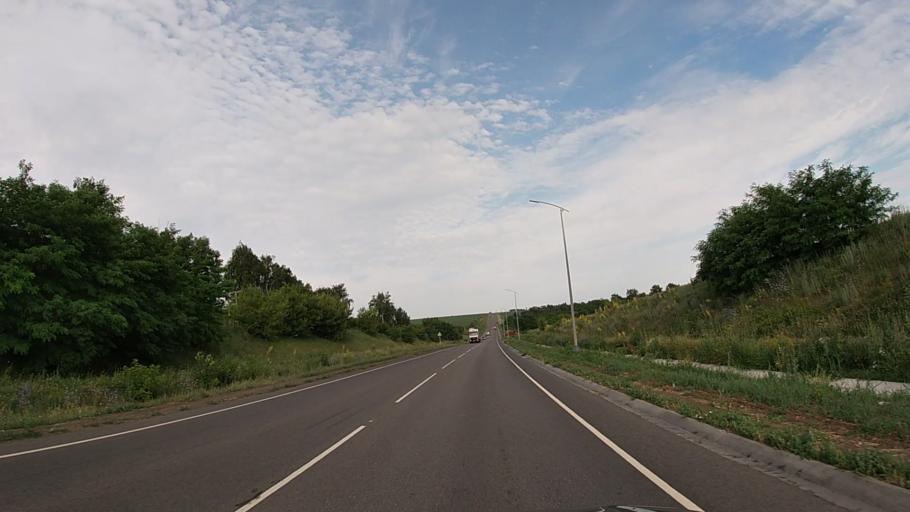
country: RU
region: Belgorod
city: Severnyy
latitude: 50.6643
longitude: 36.5246
